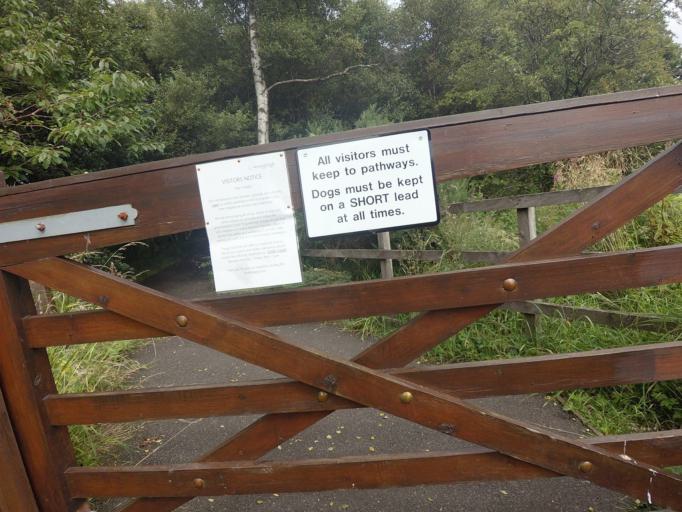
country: GB
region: Scotland
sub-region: West Lothian
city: West Calder
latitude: 55.8866
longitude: -3.5694
